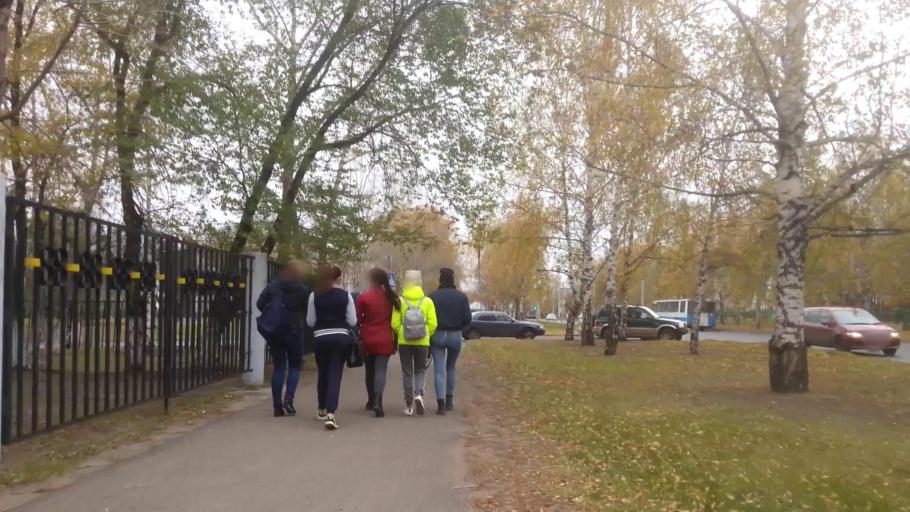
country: RU
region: Altai Krai
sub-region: Gorod Barnaulskiy
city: Barnaul
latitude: 53.3653
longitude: 83.7168
